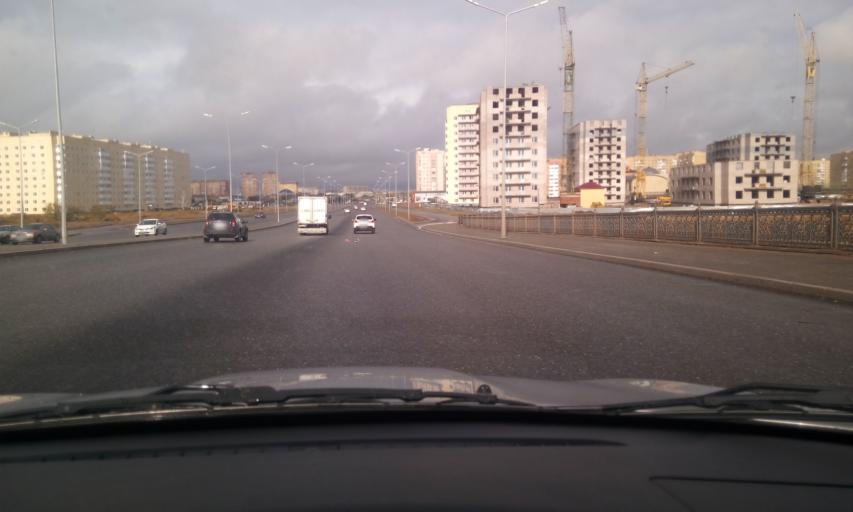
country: KZ
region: Astana Qalasy
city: Astana
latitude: 51.1660
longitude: 71.3753
